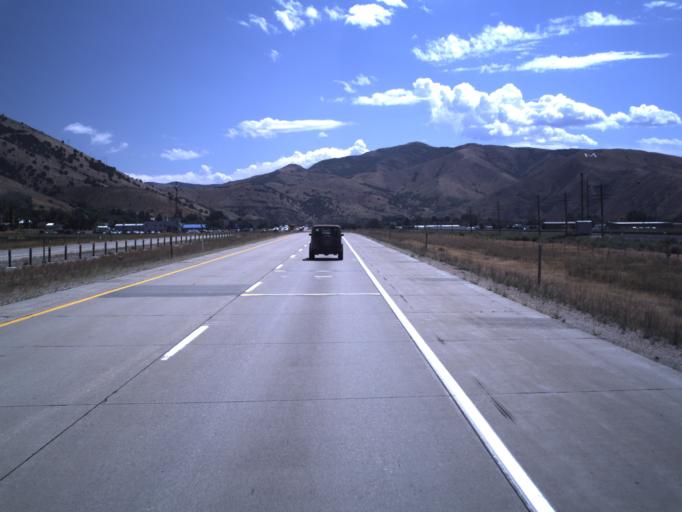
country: US
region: Utah
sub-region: Morgan County
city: Morgan
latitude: 41.0524
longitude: -111.6874
